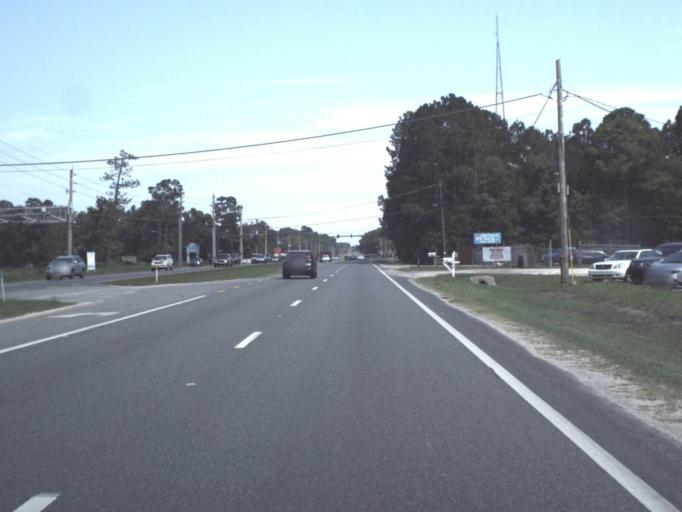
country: US
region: Florida
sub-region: Saint Johns County
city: Fruit Cove
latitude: 30.1607
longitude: -81.5343
